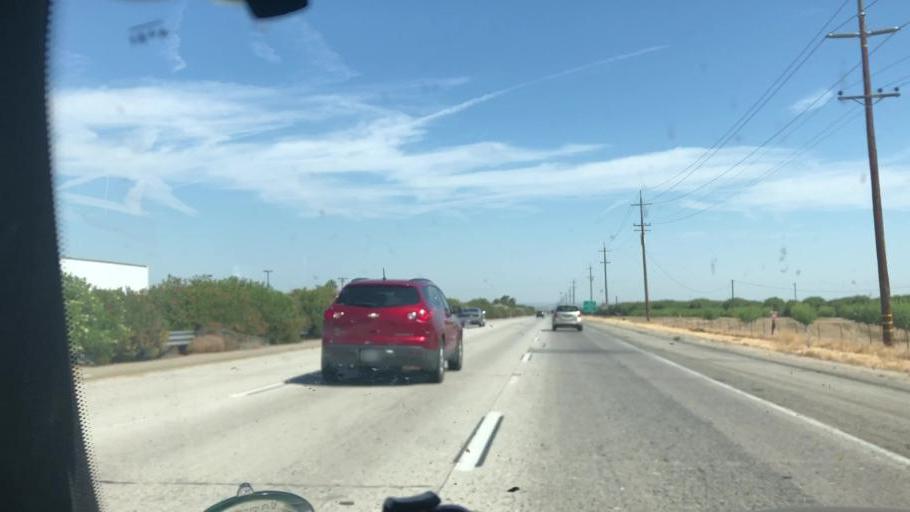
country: US
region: California
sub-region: Kern County
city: Frazier Park
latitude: 35.0316
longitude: -118.9594
